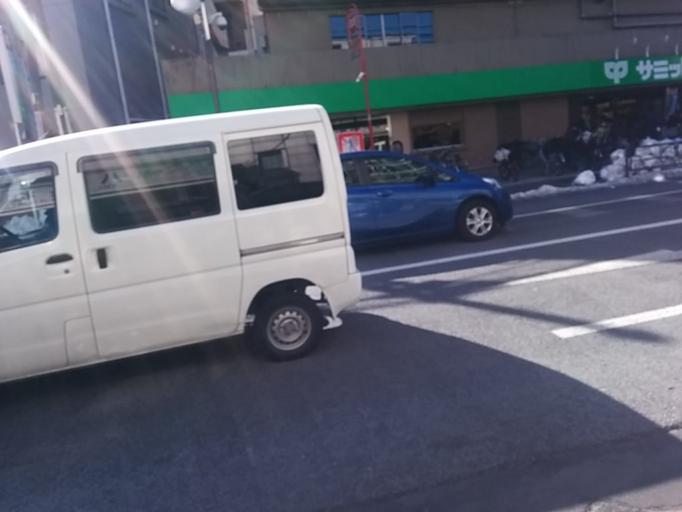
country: JP
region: Tokyo
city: Tokyo
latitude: 35.7303
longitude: 139.7617
